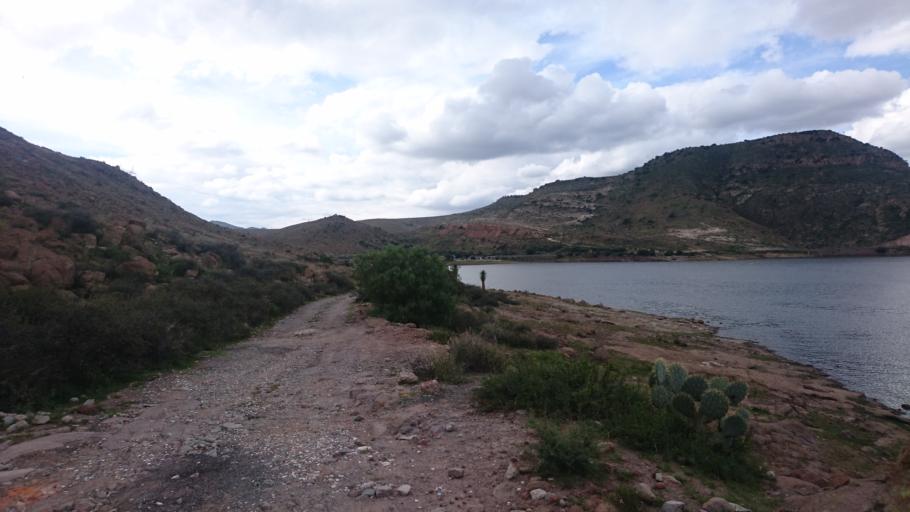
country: MX
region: San Luis Potosi
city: Escalerillas
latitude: 22.0854
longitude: -101.1009
